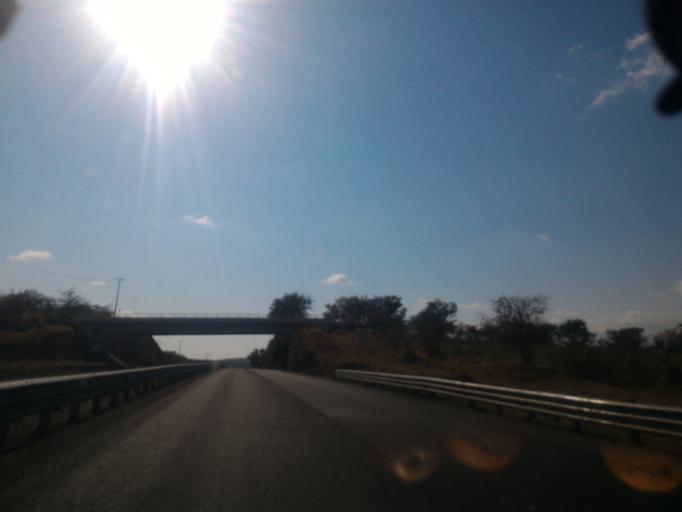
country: MX
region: Jalisco
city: Tonila
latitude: 19.4261
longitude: -103.5025
